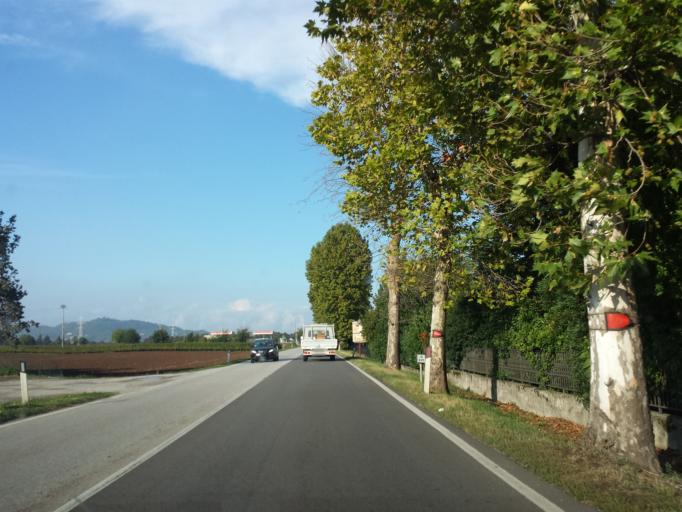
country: IT
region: Veneto
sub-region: Provincia di Vicenza
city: Montebello Vicentino
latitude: 45.4678
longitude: 11.4069
